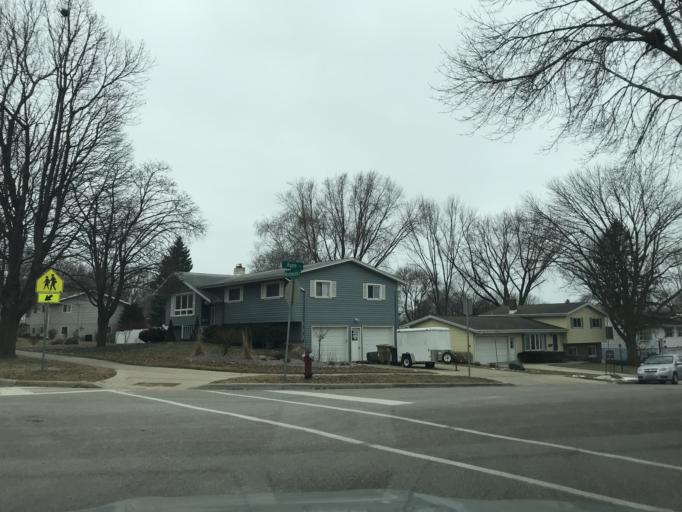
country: US
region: Wisconsin
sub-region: Dane County
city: Monona
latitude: 43.0947
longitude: -89.2982
